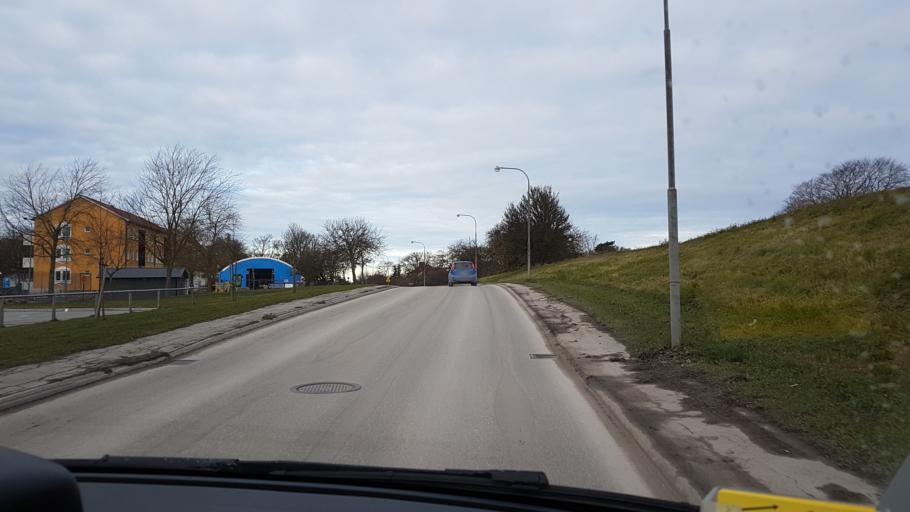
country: SE
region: Gotland
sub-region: Gotland
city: Visby
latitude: 57.6469
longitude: 18.3148
